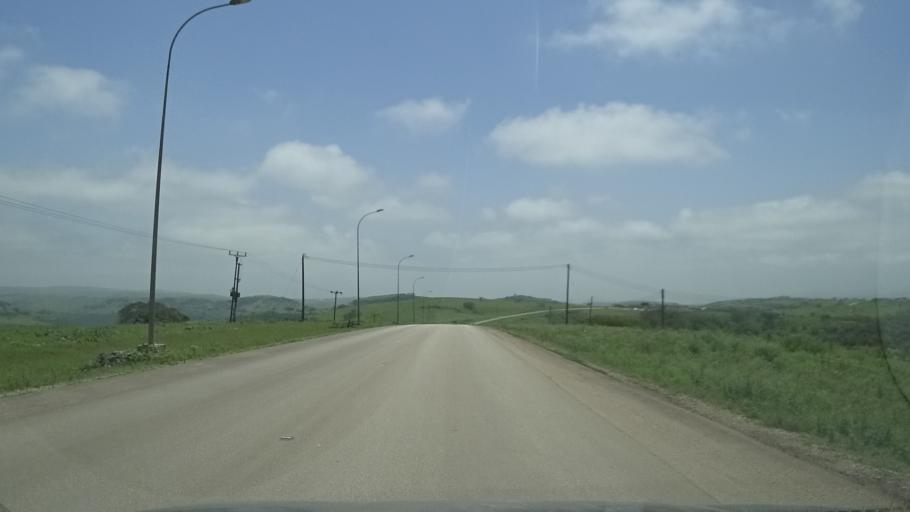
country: OM
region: Zufar
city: Salalah
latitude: 17.2278
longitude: 54.2704
